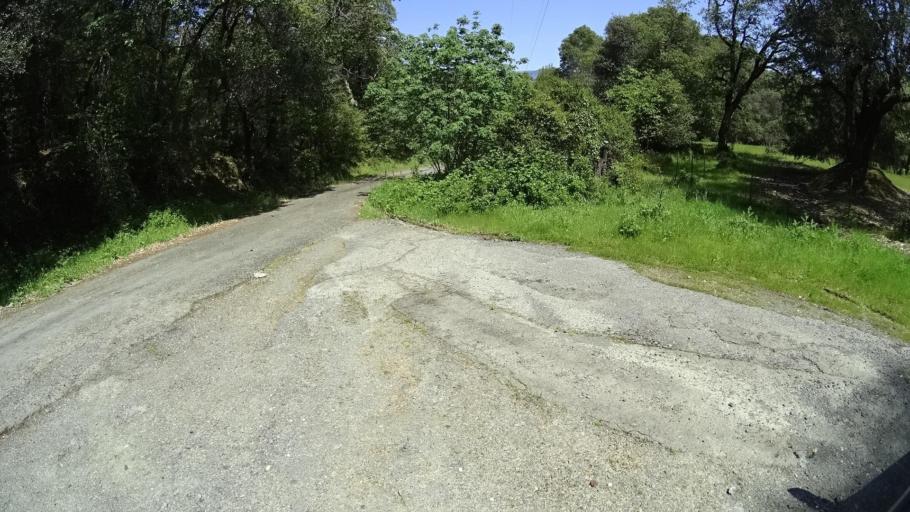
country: US
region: California
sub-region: Humboldt County
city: Redway
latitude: 40.1634
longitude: -123.6035
